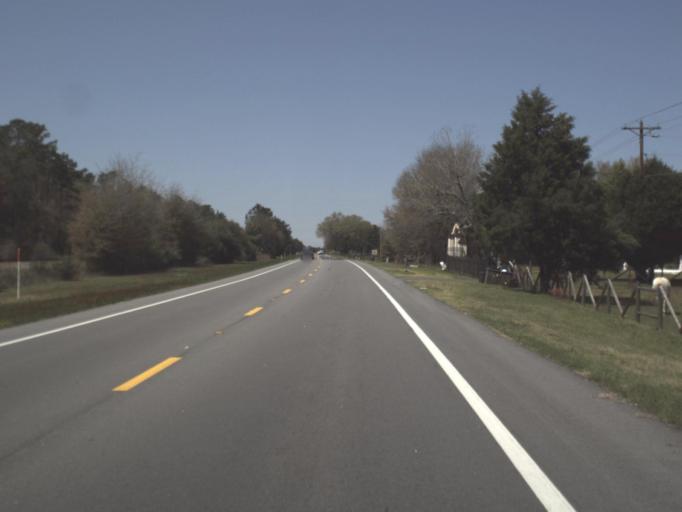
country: US
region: Florida
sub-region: Walton County
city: DeFuniak Springs
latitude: 30.7459
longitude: -86.2152
